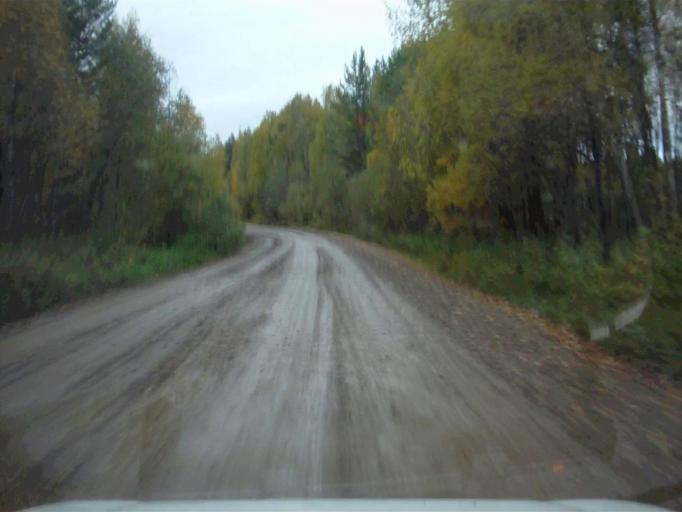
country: RU
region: Chelyabinsk
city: Nyazepetrovsk
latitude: 56.1046
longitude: 59.3851
